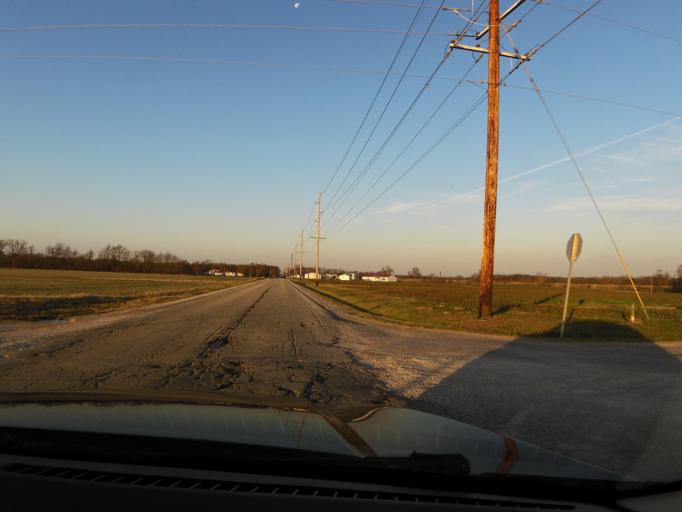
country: US
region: Illinois
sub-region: Marion County
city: Odin
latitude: 38.7650
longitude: -89.0493
